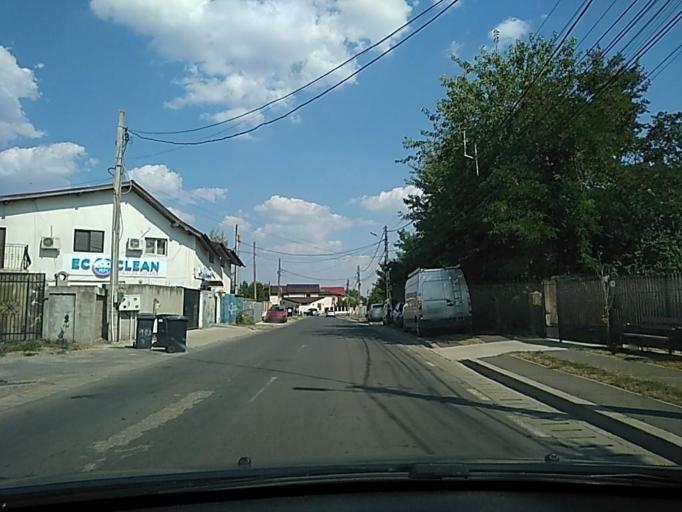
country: RO
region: Ilfov
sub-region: Comuna Domnesti
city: Domnesti
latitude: 44.4069
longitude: 25.9267
